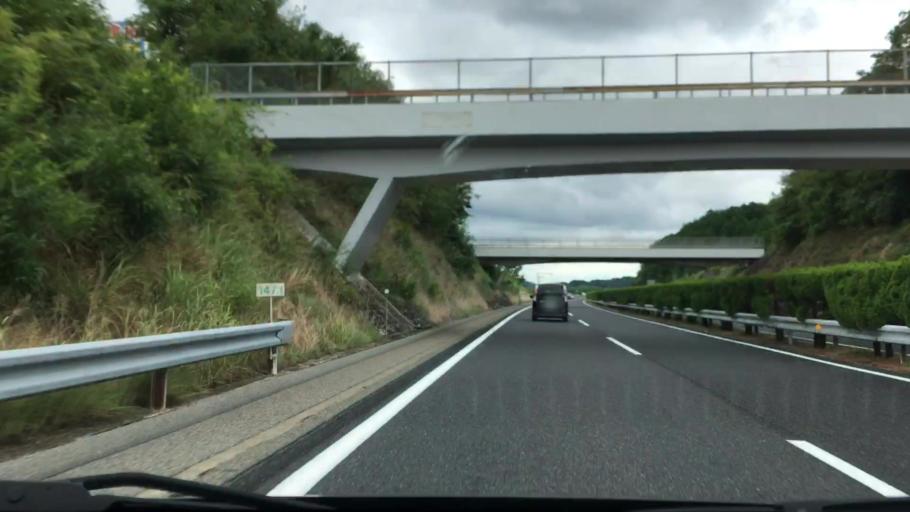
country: JP
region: Okayama
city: Tsuyama
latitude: 35.0446
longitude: 134.0855
